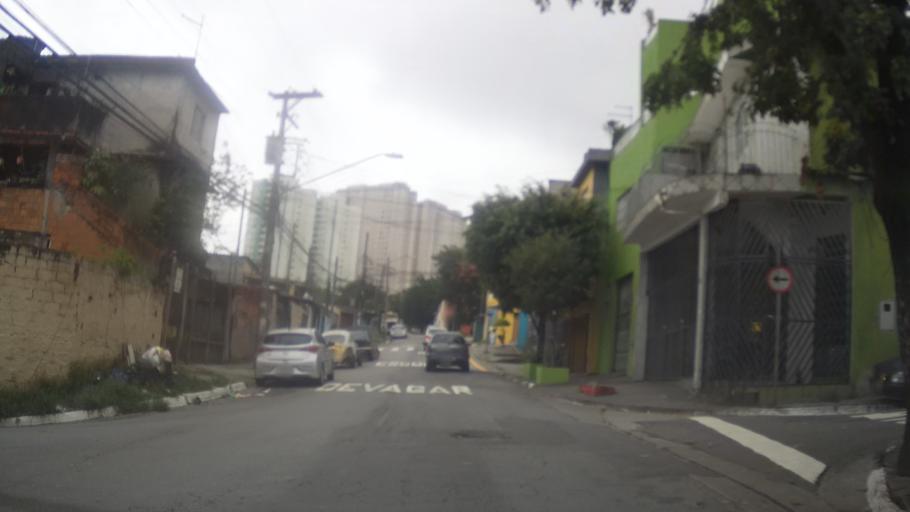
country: BR
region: Sao Paulo
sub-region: Guarulhos
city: Guarulhos
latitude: -23.4350
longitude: -46.5474
